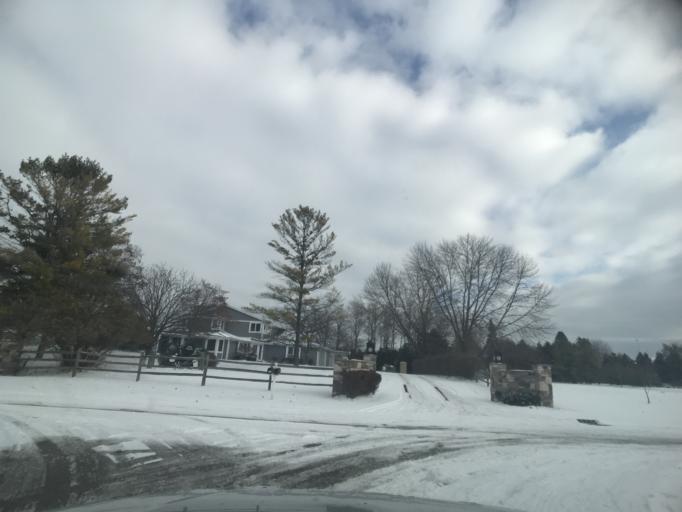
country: US
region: Wisconsin
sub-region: Door County
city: Sturgeon Bay
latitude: 44.8202
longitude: -87.3669
